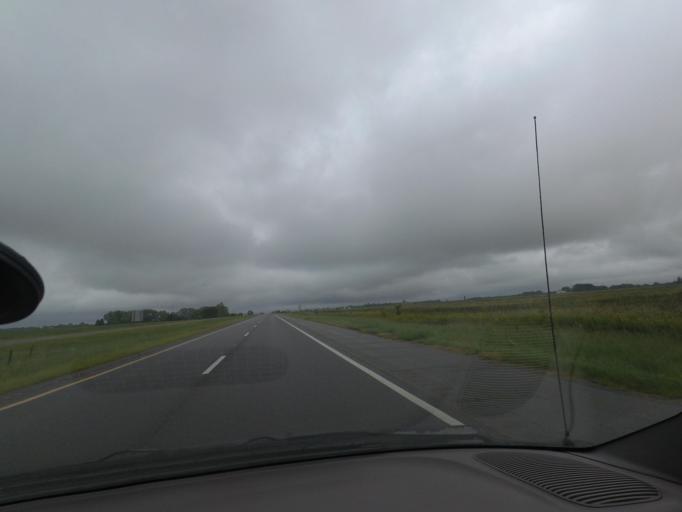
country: US
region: Illinois
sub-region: Champaign County
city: Mahomet
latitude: 40.1203
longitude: -88.3977
